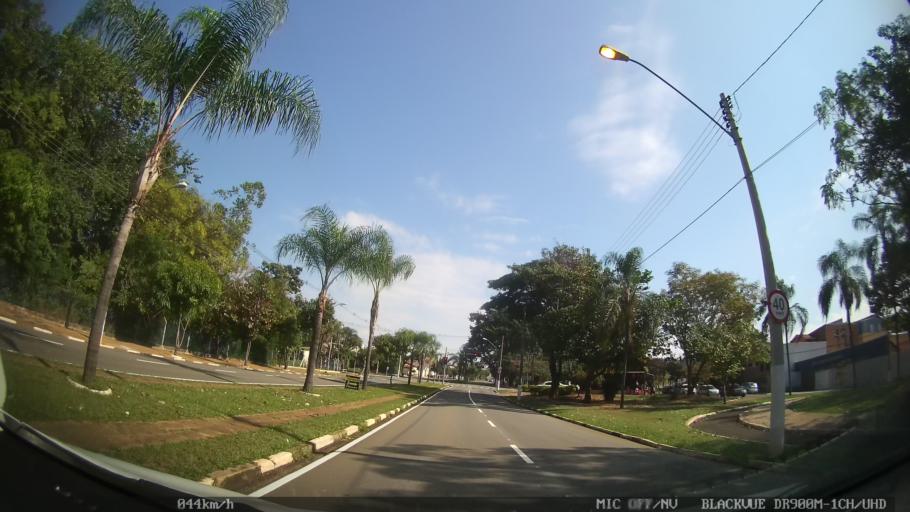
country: BR
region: Sao Paulo
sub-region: Paulinia
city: Paulinia
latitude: -22.7763
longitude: -47.1653
